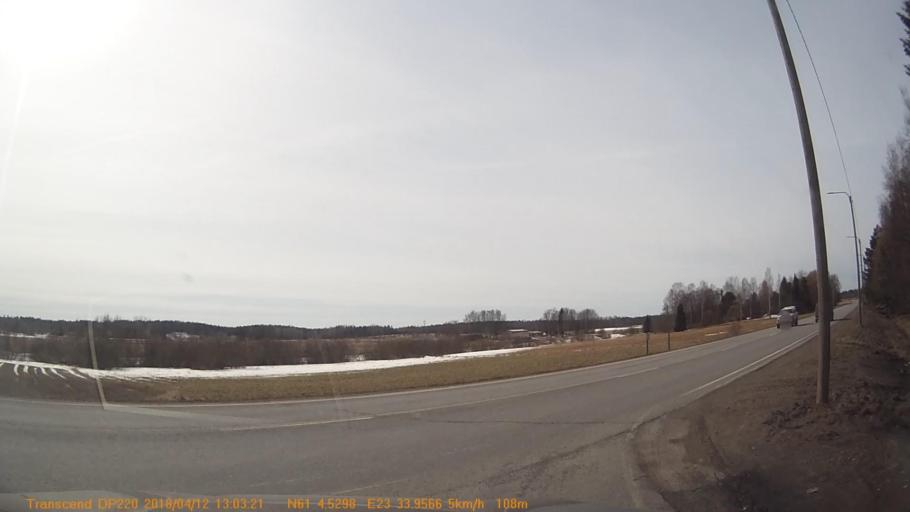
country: FI
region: Pirkanmaa
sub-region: Etelae-Pirkanmaa
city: Urjala
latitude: 61.0755
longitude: 23.5659
